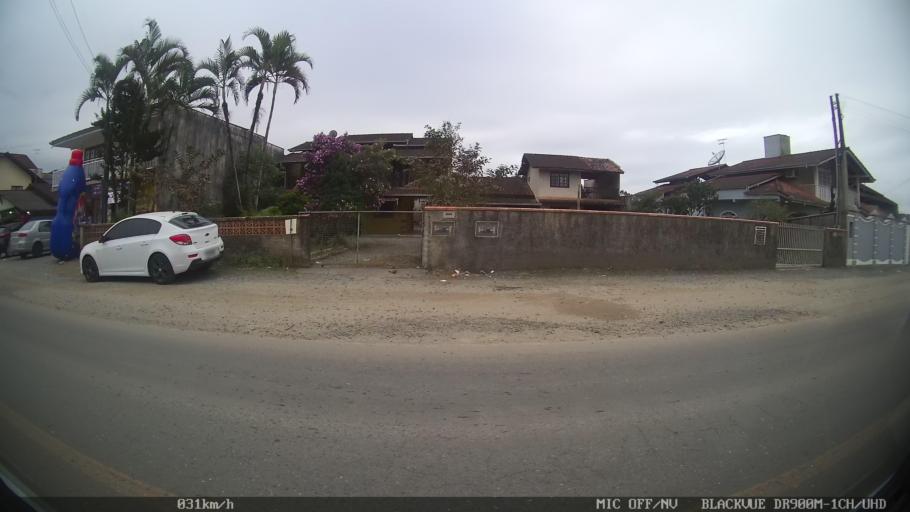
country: BR
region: Santa Catarina
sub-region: Joinville
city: Joinville
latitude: -26.3370
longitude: -48.9021
